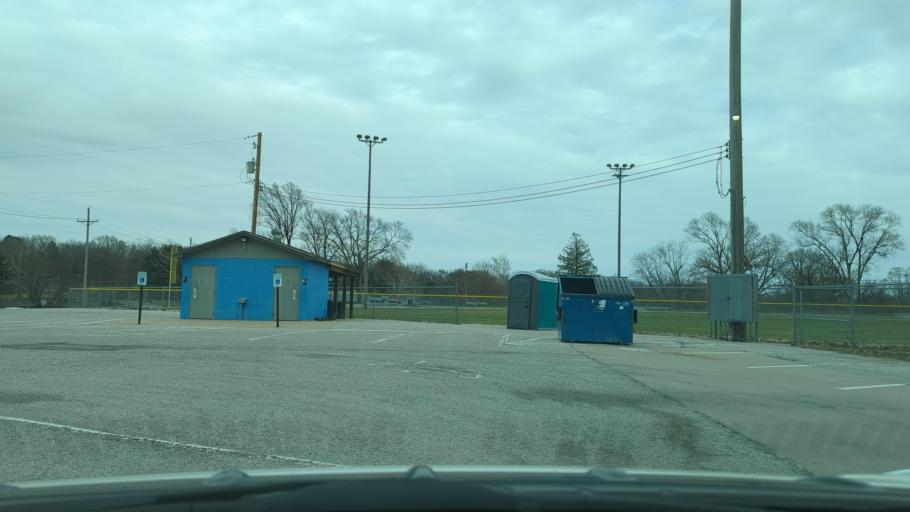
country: US
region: Nebraska
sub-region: Sarpy County
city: Bellevue
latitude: 41.1397
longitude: -95.9105
